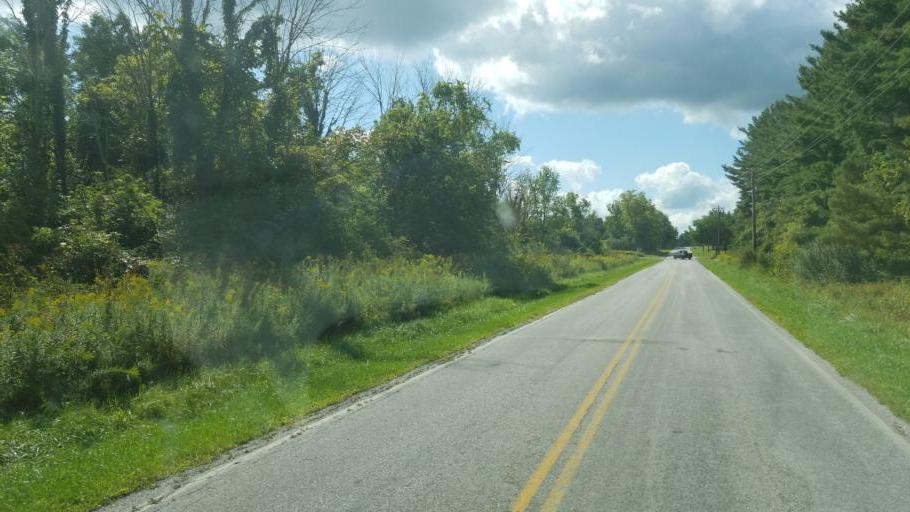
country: US
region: Ohio
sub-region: Medina County
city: Lodi
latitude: 41.1140
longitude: -82.0941
